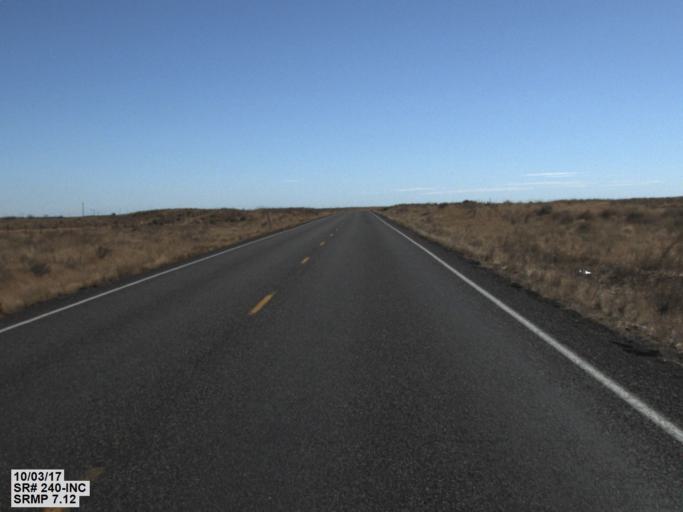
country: US
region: Washington
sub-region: Benton County
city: Benton City
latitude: 46.5066
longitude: -119.6327
